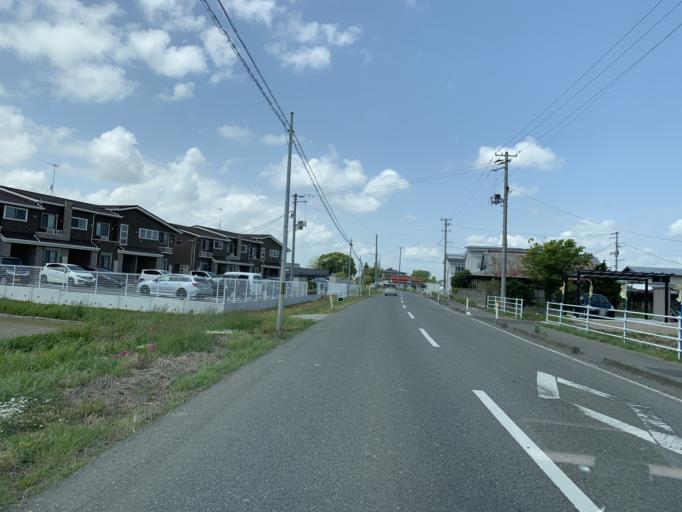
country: JP
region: Miyagi
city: Wakuya
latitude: 38.7054
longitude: 141.2217
